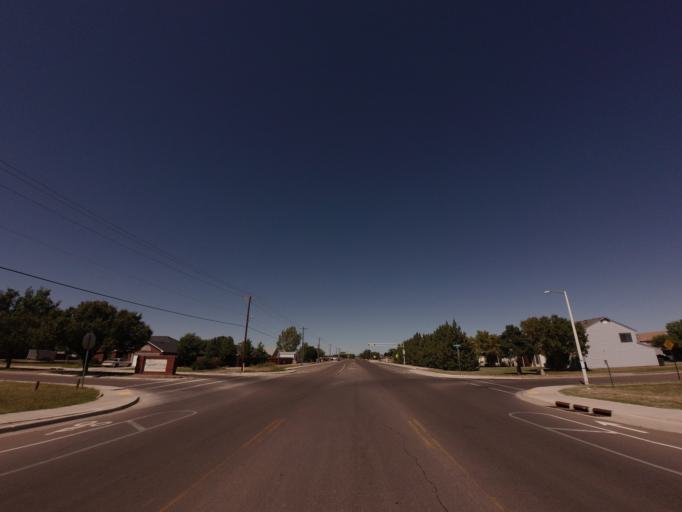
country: US
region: New Mexico
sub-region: Curry County
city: Clovis
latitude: 34.4454
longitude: -103.1785
